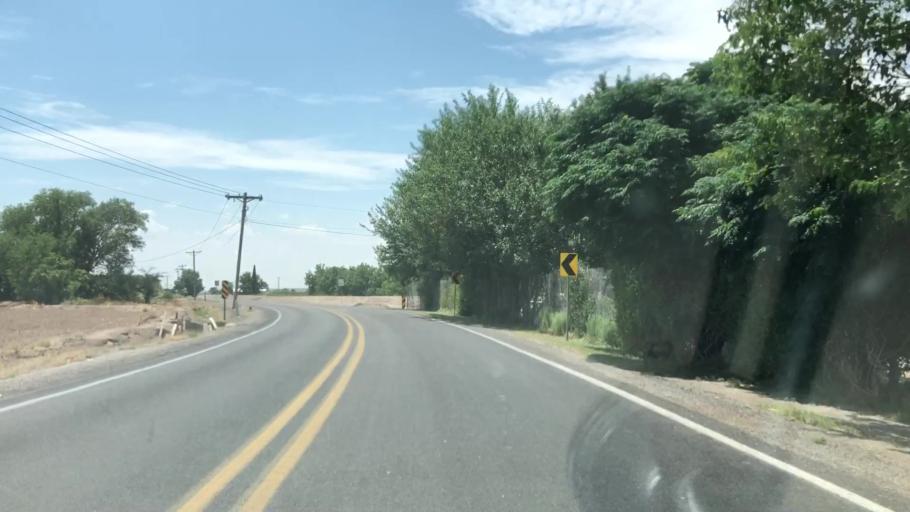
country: US
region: New Mexico
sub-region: Dona Ana County
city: Vado
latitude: 32.0896
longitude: -106.6834
